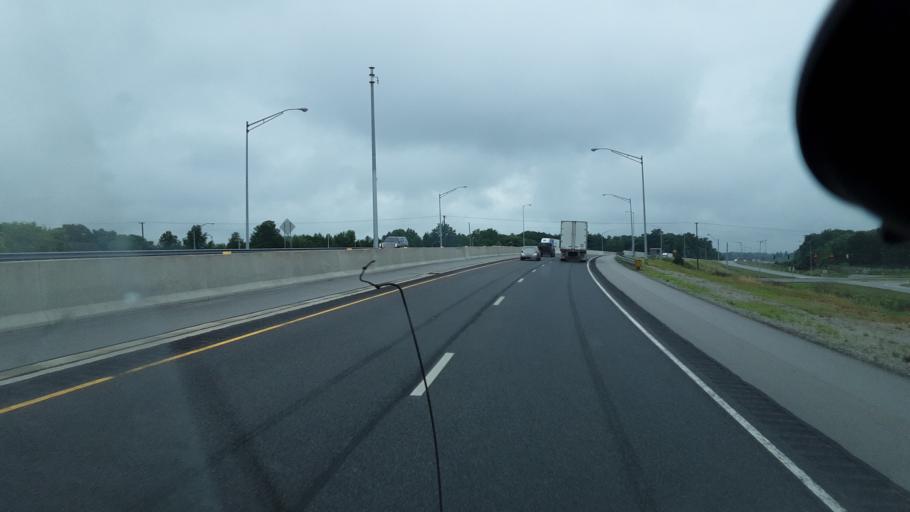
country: US
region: Indiana
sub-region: Allen County
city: New Haven
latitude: 40.9830
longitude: -85.0838
